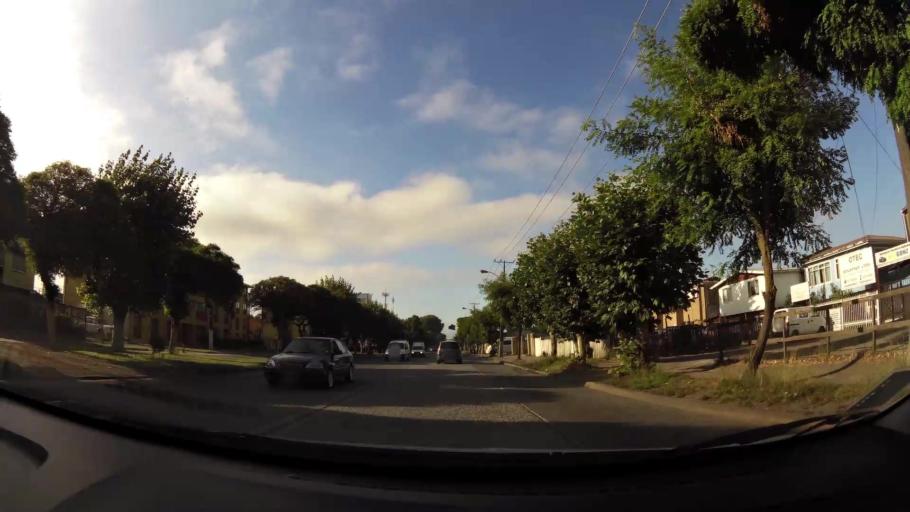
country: CL
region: Biobio
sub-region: Provincia de Concepcion
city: Concepcion
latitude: -36.7882
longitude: -73.0869
